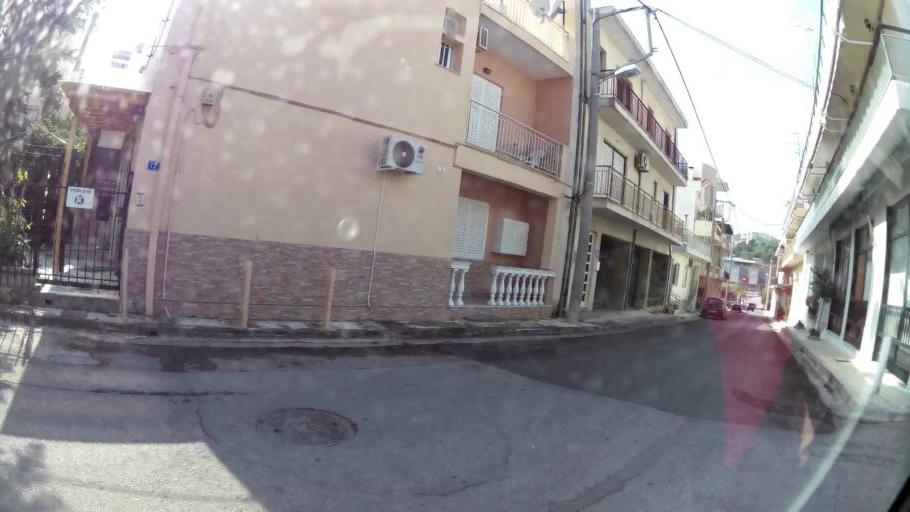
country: GR
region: Attica
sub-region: Nomarchia Dytikis Attikis
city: Zefyri
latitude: 38.0632
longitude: 23.7168
